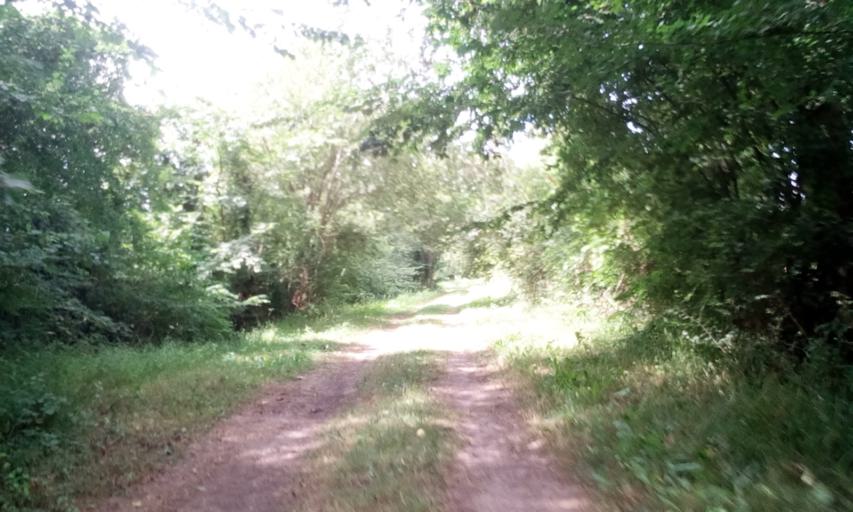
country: FR
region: Lower Normandy
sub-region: Departement du Calvados
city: Sannerville
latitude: 49.1572
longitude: -0.2071
